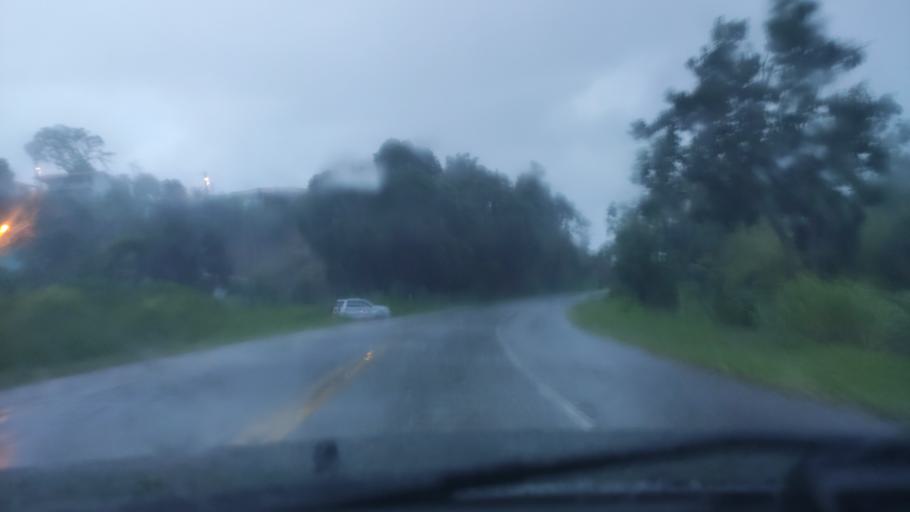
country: BR
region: Sao Paulo
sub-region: Socorro
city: Socorro
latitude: -22.7656
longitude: -46.5589
